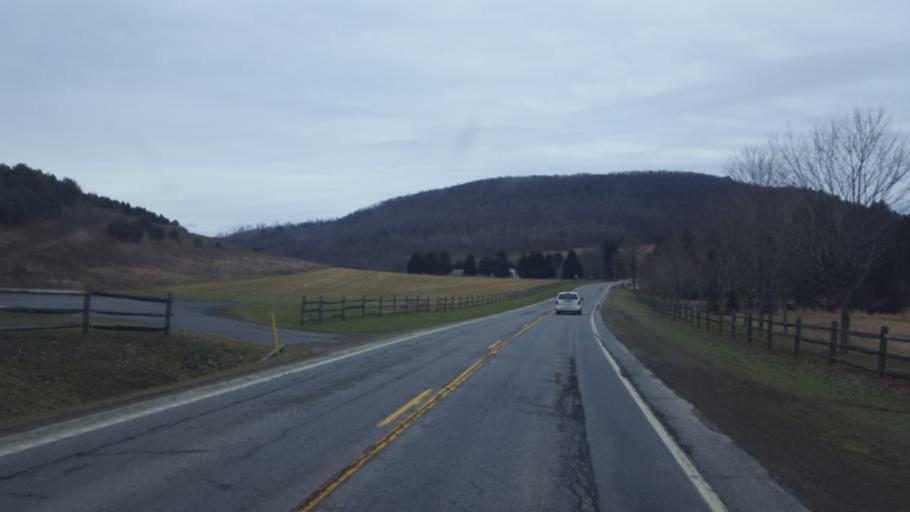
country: US
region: Pennsylvania
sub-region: Potter County
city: Coudersport
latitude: 41.8338
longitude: -77.9466
